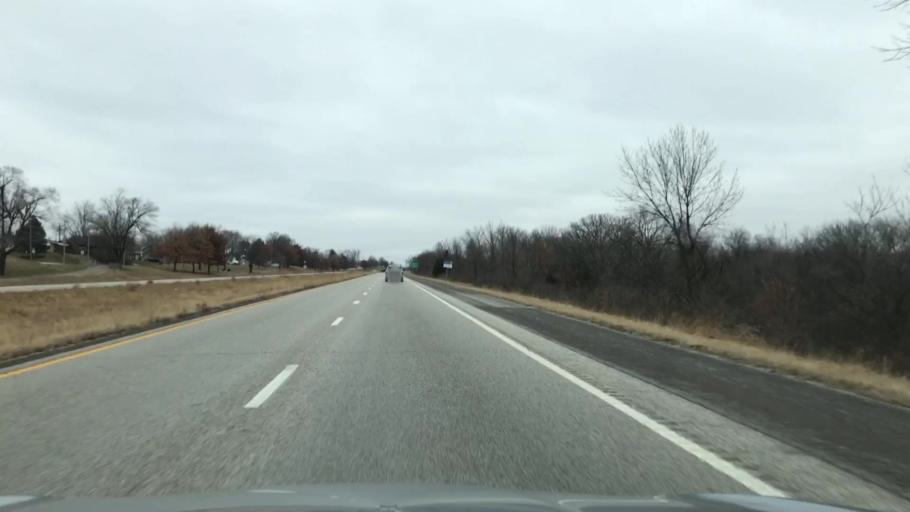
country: US
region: Missouri
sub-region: Clay County
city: Liberty
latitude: 39.2203
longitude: -94.4097
